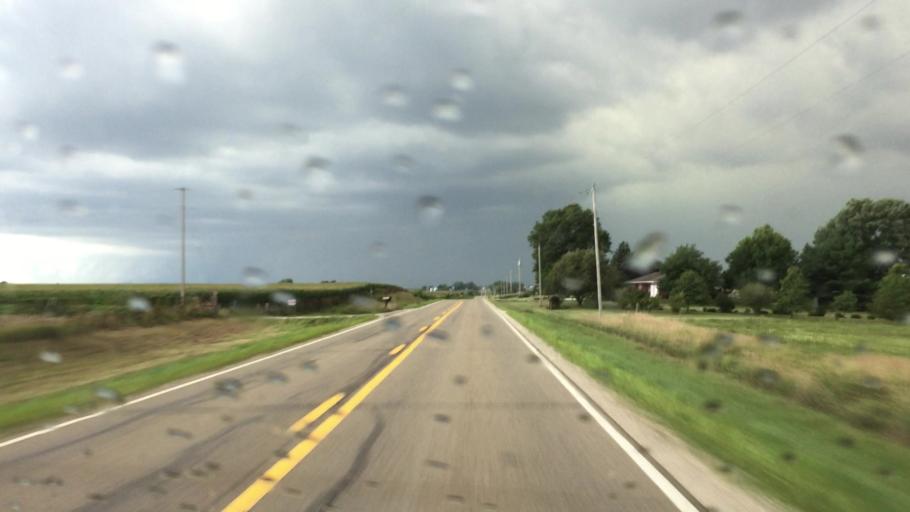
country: US
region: Iowa
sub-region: Henry County
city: Mount Pleasant
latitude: 40.7843
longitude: -91.5237
